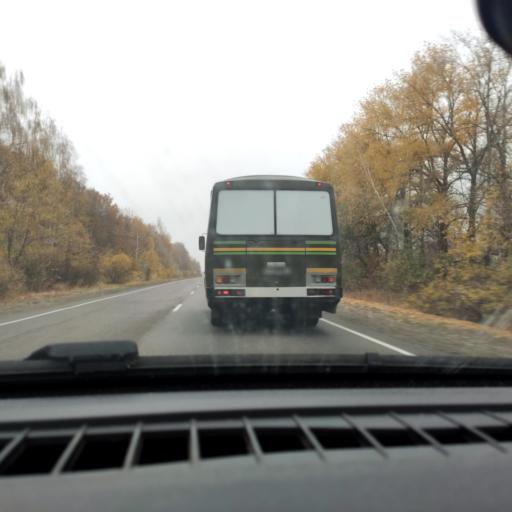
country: RU
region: Voronezj
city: Kolodeznyy
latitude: 51.3581
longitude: 39.0236
